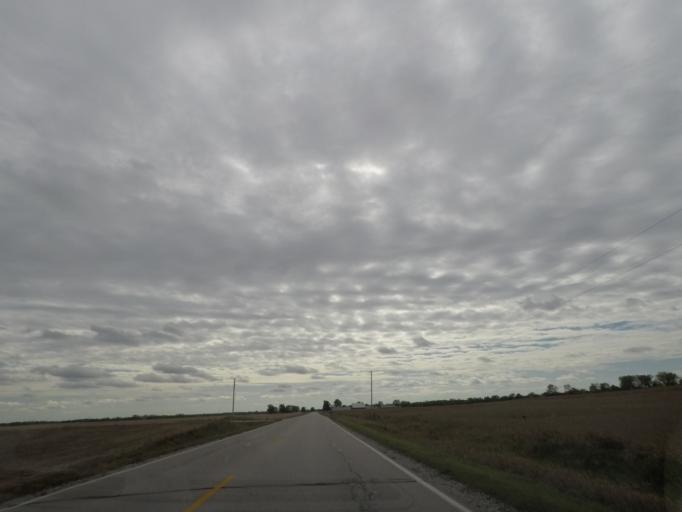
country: US
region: Iowa
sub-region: Story County
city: Huxley
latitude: 41.8554
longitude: -93.5316
